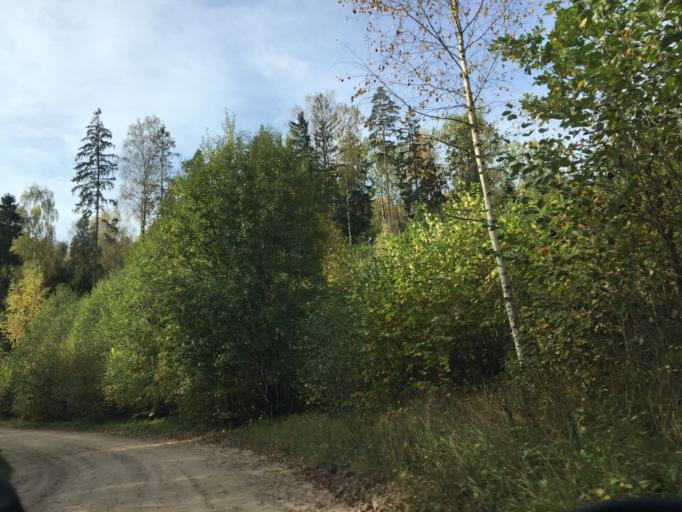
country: LV
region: Jaunpils
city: Jaunpils
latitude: 56.6157
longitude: 23.0239
